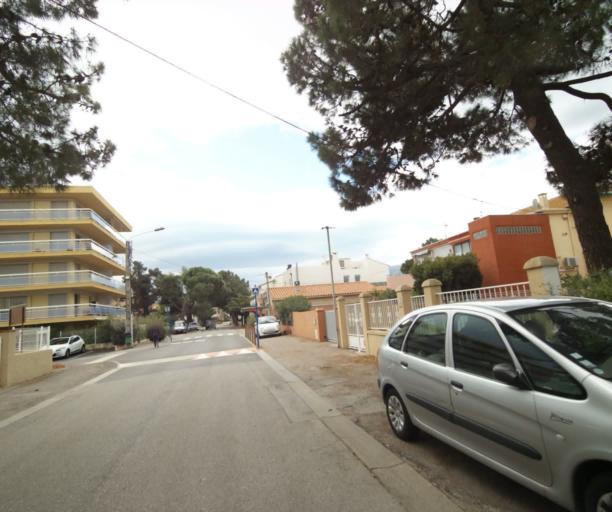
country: FR
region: Languedoc-Roussillon
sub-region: Departement des Pyrenees-Orientales
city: Argelers
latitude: 42.5586
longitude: 3.0458
